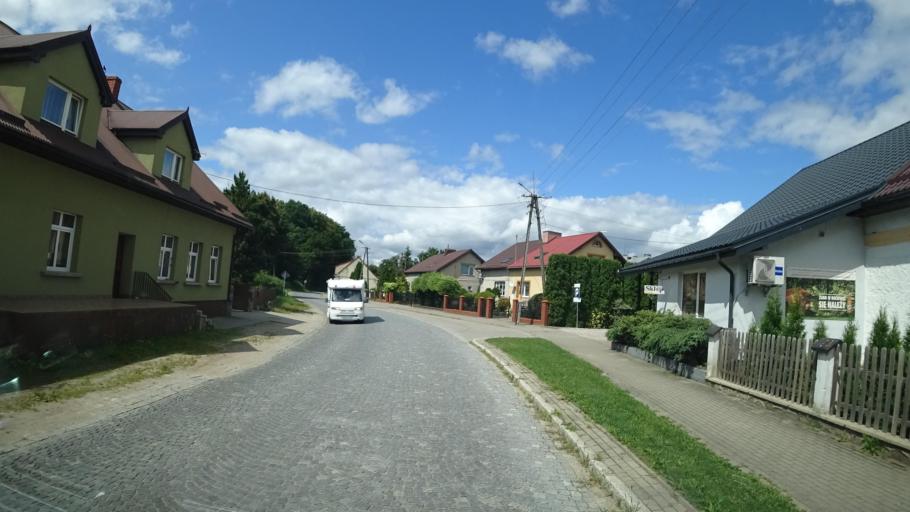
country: PL
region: Warmian-Masurian Voivodeship
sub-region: Powiat goldapski
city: Banie Mazurskie
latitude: 54.2170
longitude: 22.1554
